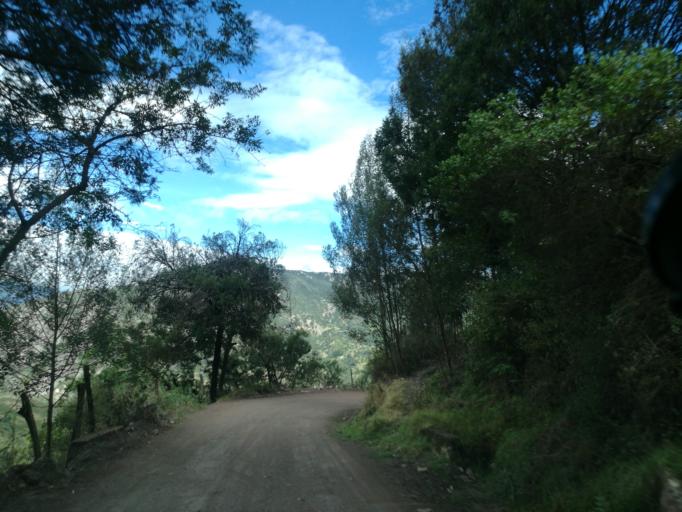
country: CO
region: Boyaca
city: Susacon
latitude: 6.1229
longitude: -72.7114
